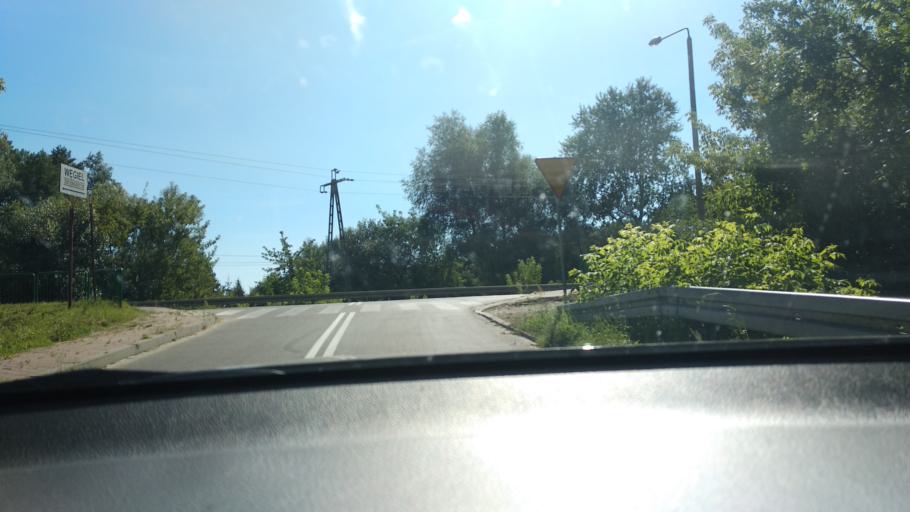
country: PL
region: Masovian Voivodeship
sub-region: Powiat pultuski
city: Pultusk
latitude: 52.6952
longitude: 21.0978
